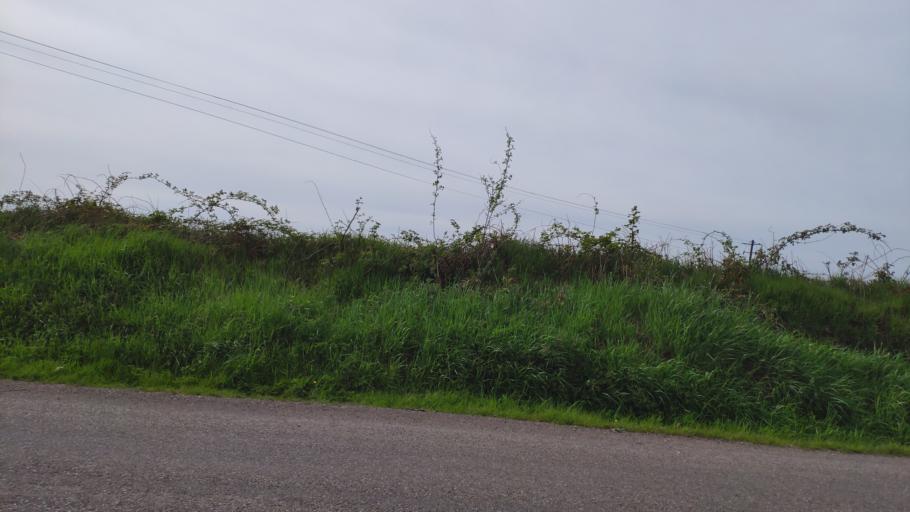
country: IE
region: Munster
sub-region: County Cork
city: Blarney
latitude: 51.9912
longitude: -8.5017
